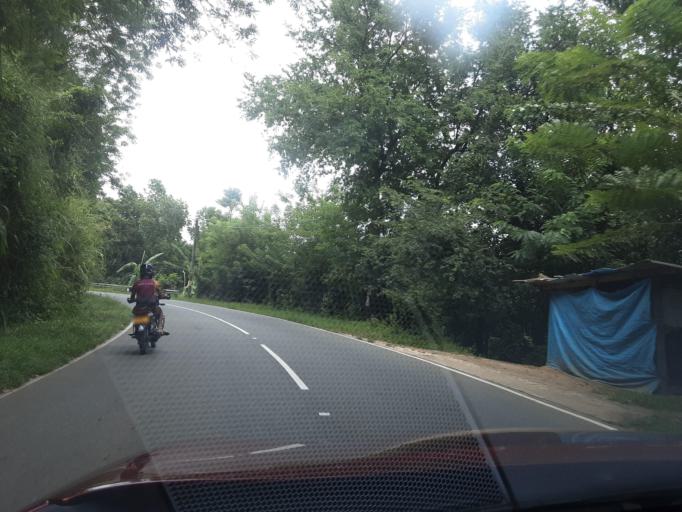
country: LK
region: Uva
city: Monaragala
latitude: 6.8991
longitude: 81.2514
